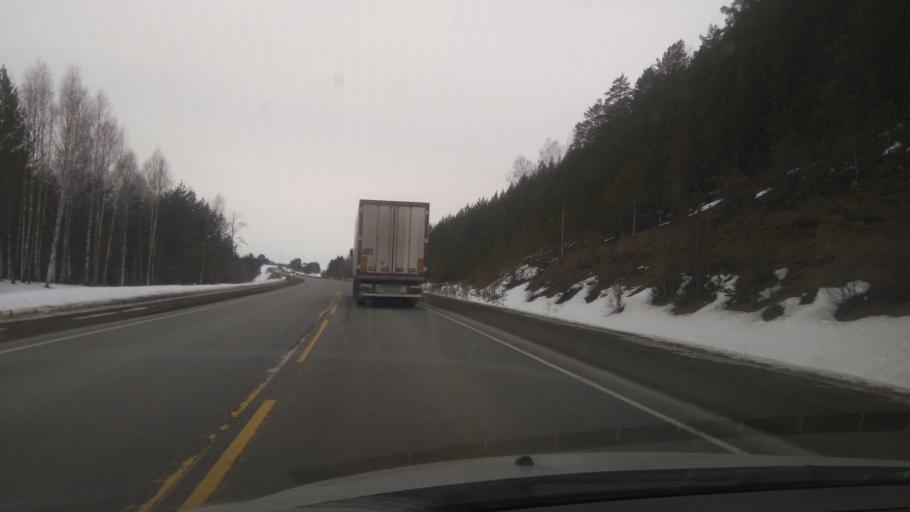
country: RU
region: Sverdlovsk
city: Ufimskiy
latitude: 56.7746
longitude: 58.2216
